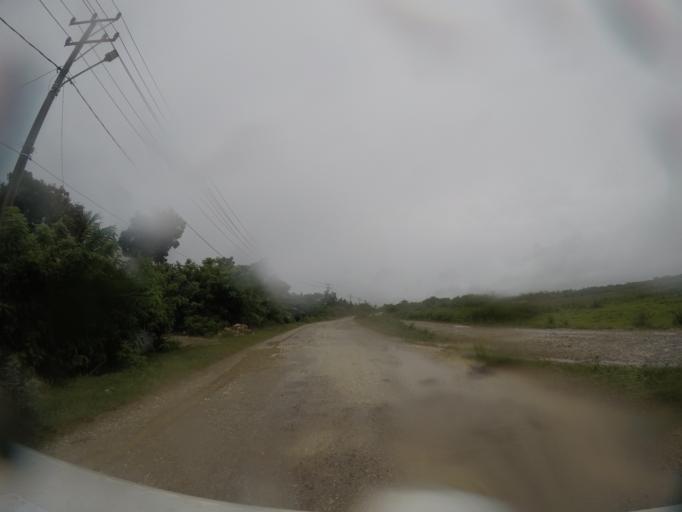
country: TL
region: Lautem
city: Lospalos
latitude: -8.5089
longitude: 127.0050
